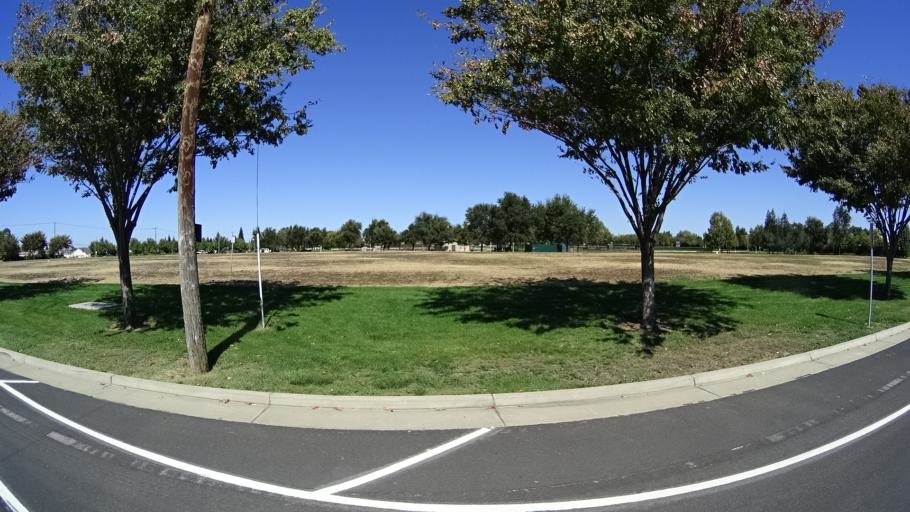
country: US
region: California
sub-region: Sacramento County
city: Elk Grove
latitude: 38.4381
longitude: -121.3697
